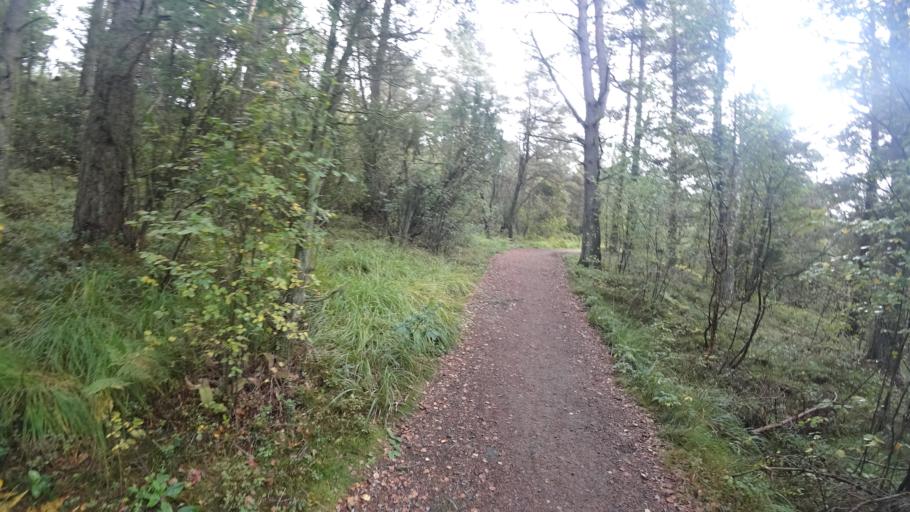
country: SE
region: Vaestra Goetaland
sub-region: Molndal
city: Moelndal
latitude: 57.6188
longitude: 11.9732
